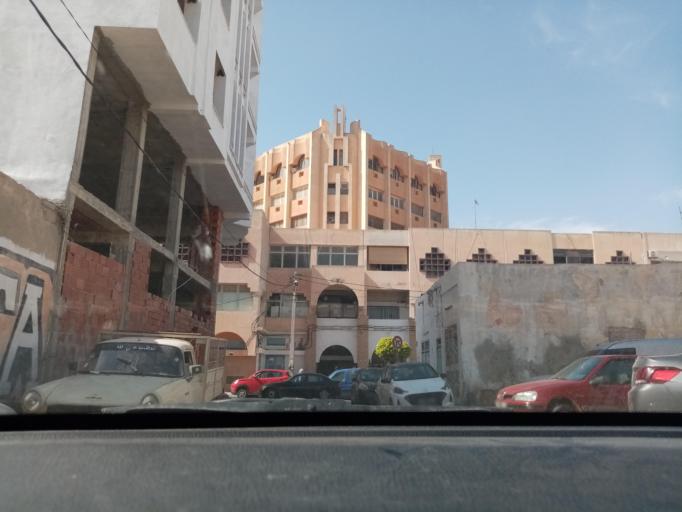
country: TN
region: Qabis
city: Gabes
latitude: 33.8869
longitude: 10.1039
